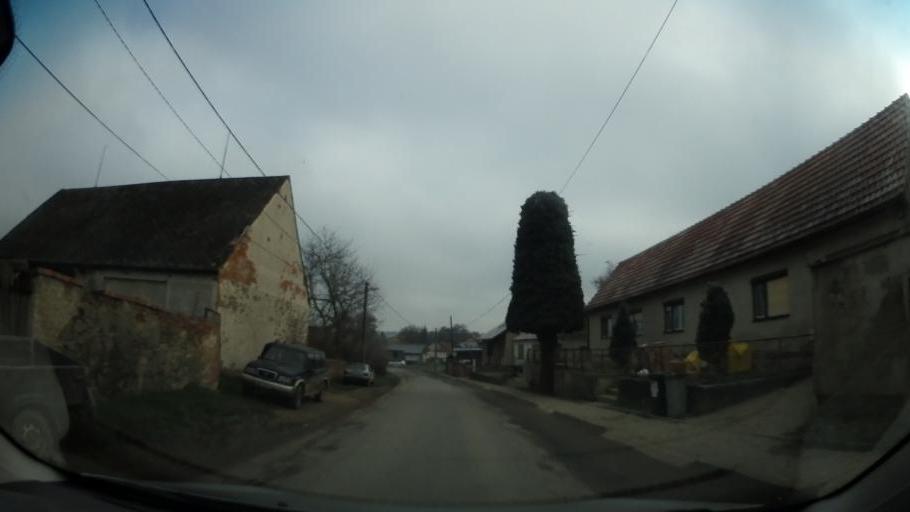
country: CZ
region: Vysocina
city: Mohelno
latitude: 49.1240
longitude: 16.2419
